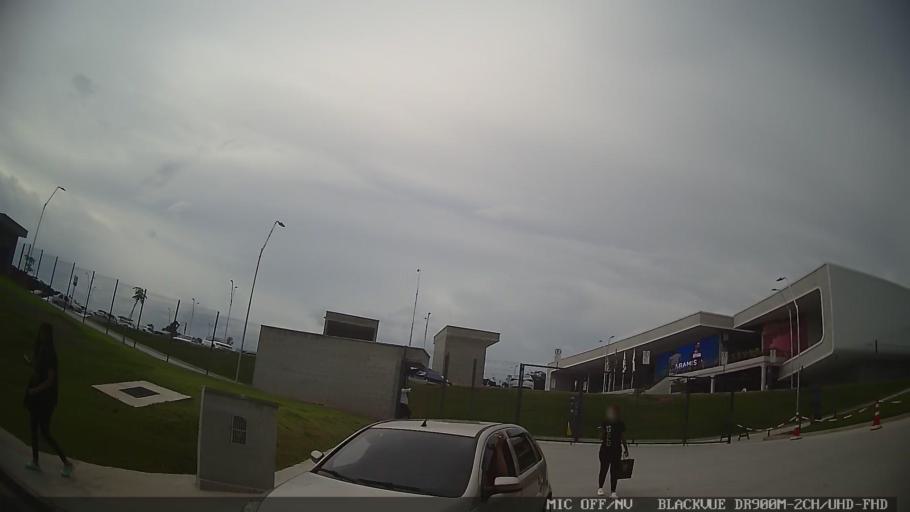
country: BR
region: Sao Paulo
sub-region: Aruja
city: Aruja
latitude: -23.4319
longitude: -46.2729
